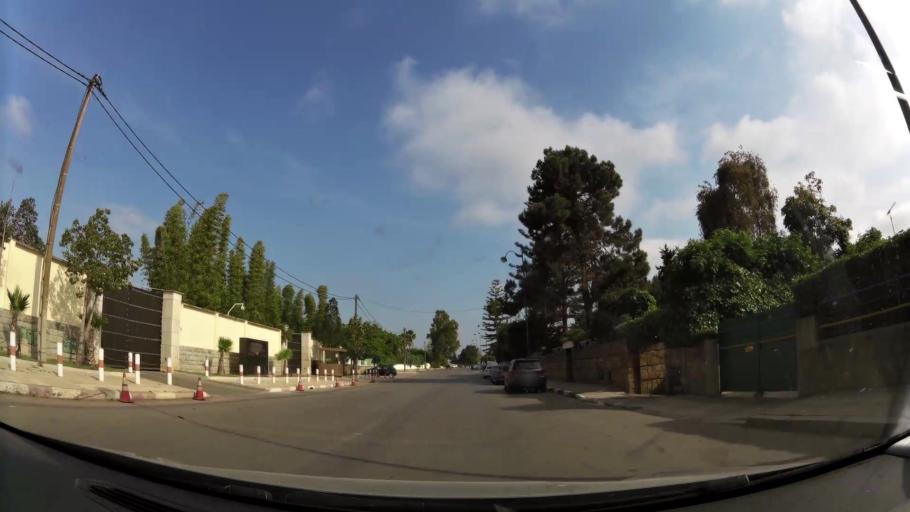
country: MA
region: Rabat-Sale-Zemmour-Zaer
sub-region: Rabat
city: Rabat
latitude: 33.9682
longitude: -6.8387
